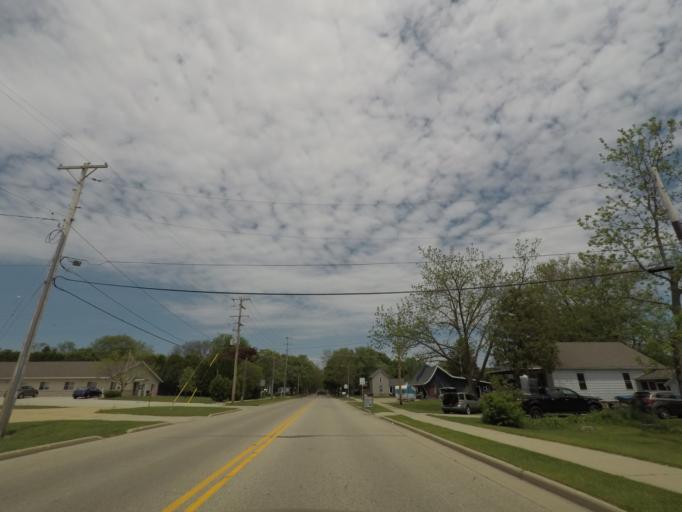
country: US
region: Wisconsin
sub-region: Rock County
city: Evansville
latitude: 42.7721
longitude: -89.2991
